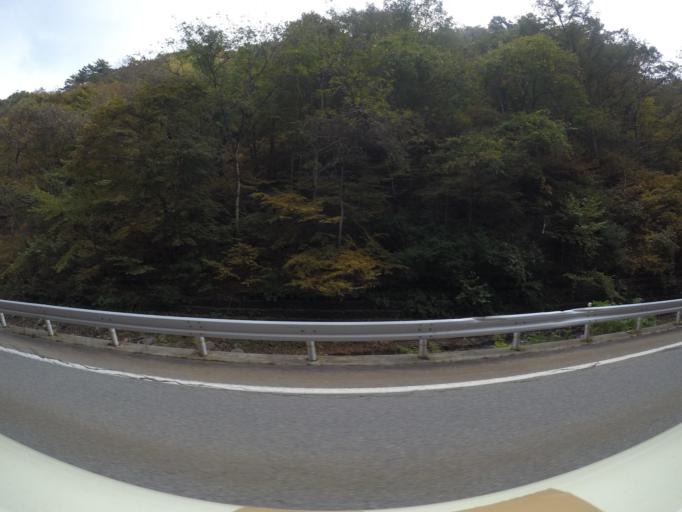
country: JP
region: Nagano
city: Ina
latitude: 35.9051
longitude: 137.7780
